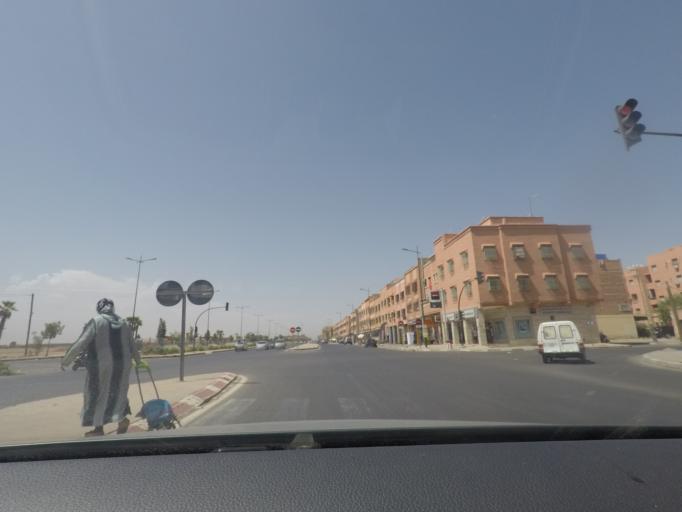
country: MA
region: Marrakech-Tensift-Al Haouz
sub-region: Marrakech
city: Marrakesh
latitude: 31.5860
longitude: -8.0436
